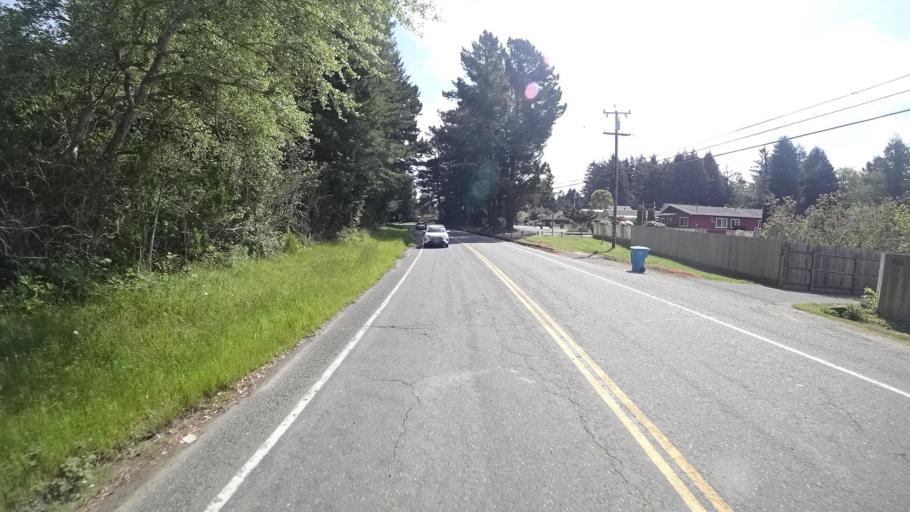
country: US
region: California
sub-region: Humboldt County
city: Pine Hills
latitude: 40.7334
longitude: -124.1525
